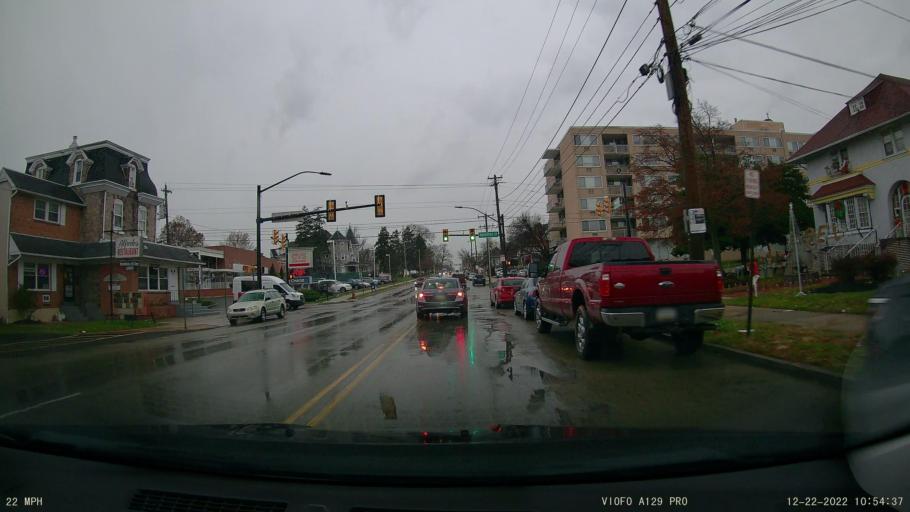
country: US
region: Pennsylvania
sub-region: Montgomery County
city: Norristown
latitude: 40.1216
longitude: -75.3590
